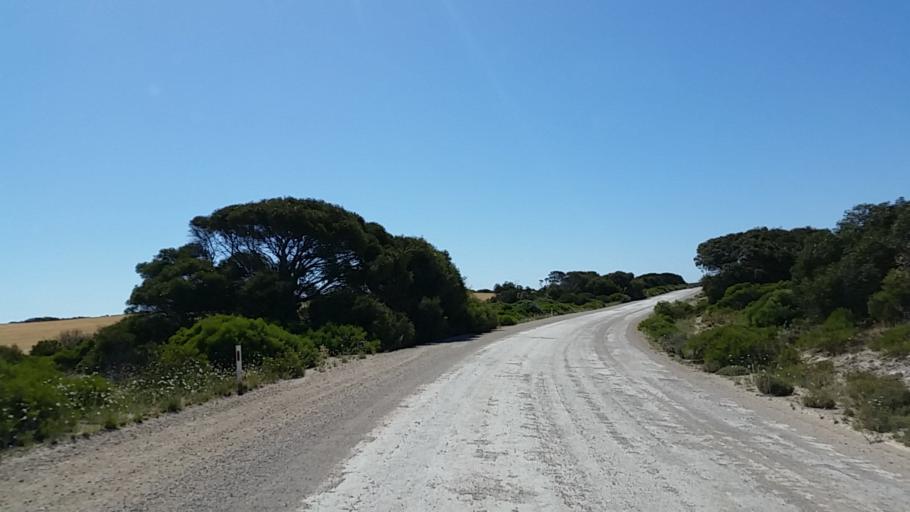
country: AU
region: South Australia
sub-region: Yorke Peninsula
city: Honiton
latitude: -35.2299
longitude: 137.1095
